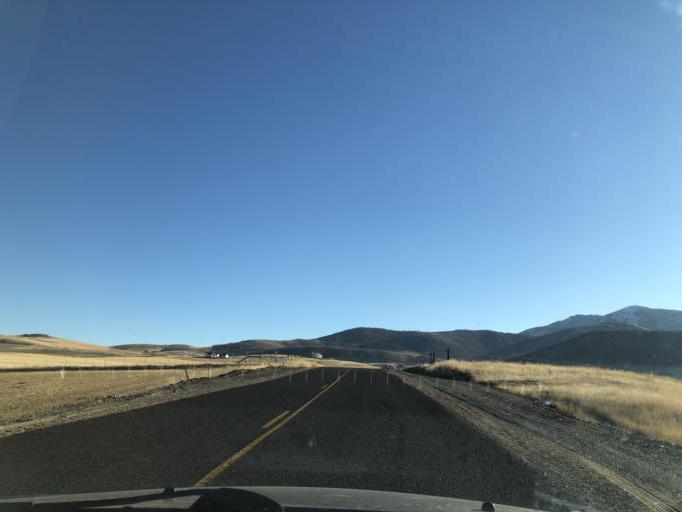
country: US
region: Utah
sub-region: Cache County
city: Wellsville
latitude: 41.5947
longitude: -111.9279
